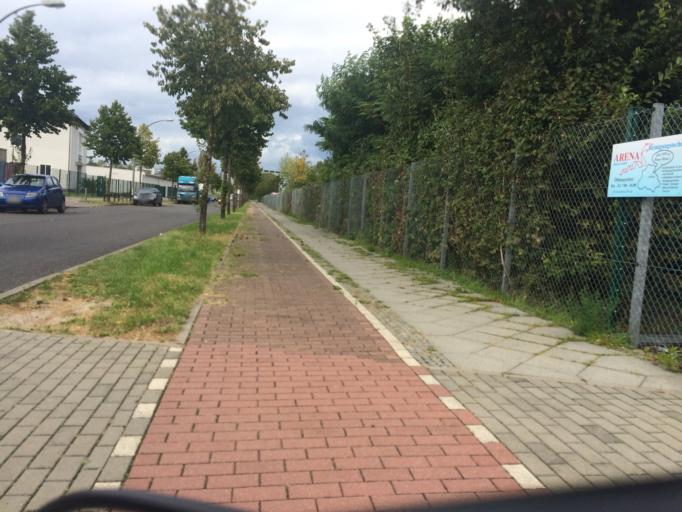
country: DE
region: Berlin
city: Lichtenberg
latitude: 52.5275
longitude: 13.4965
